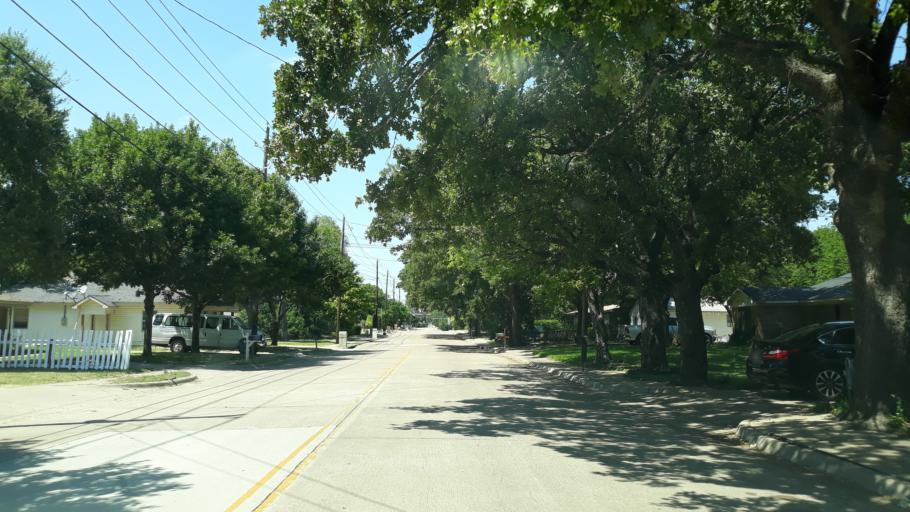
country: US
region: Texas
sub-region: Dallas County
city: Irving
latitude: 32.8196
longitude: -97.0024
